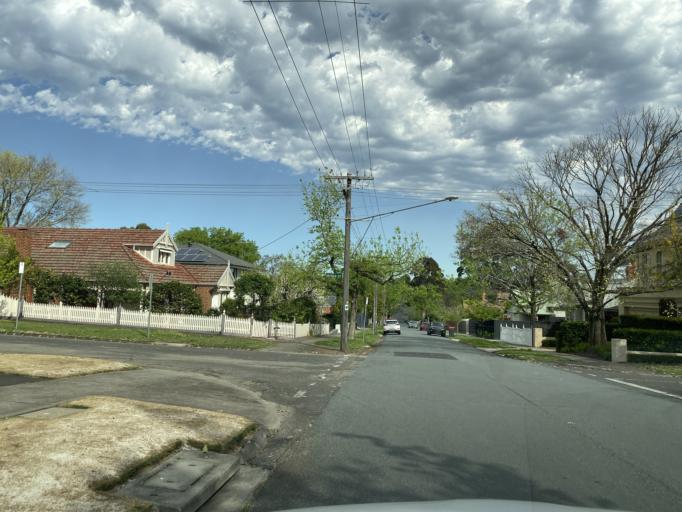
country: AU
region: Victoria
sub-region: Boroondara
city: Canterbury
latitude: -37.8283
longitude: 145.0762
